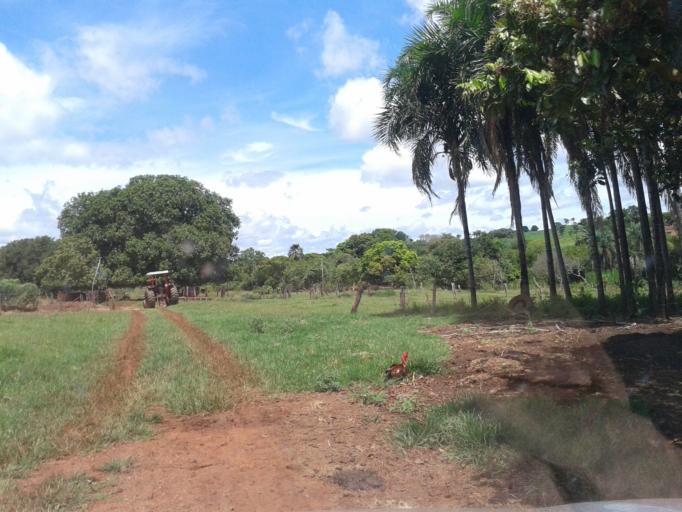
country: BR
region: Minas Gerais
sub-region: Santa Vitoria
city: Santa Vitoria
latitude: -18.7880
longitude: -49.8570
